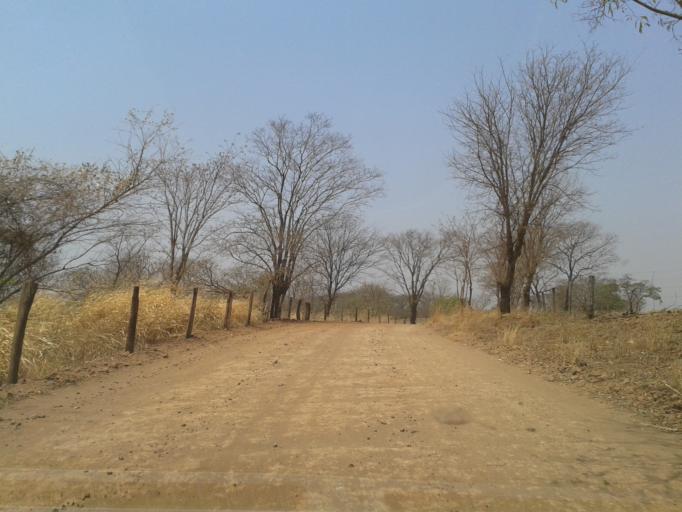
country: BR
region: Minas Gerais
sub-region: Centralina
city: Centralina
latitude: -18.7089
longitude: -49.2327
